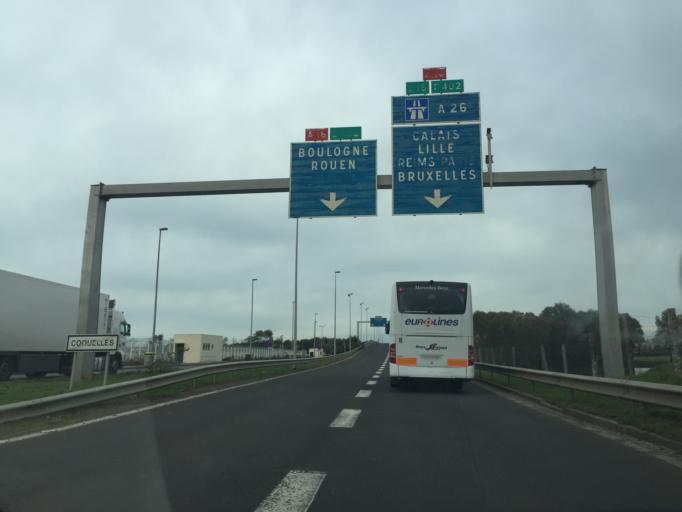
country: FR
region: Nord-Pas-de-Calais
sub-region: Departement du Pas-de-Calais
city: Coquelles
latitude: 50.9358
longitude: 1.8183
